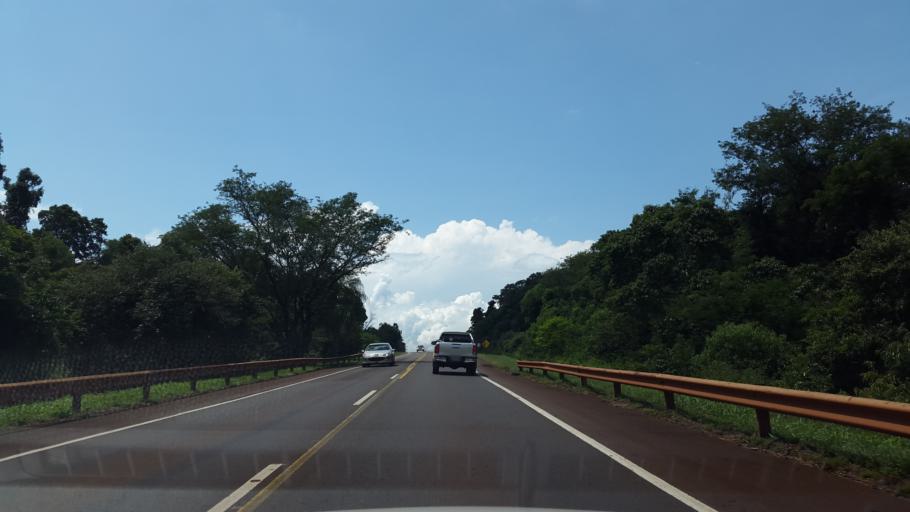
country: AR
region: Misiones
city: El Alcazar
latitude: -26.7001
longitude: -54.8379
